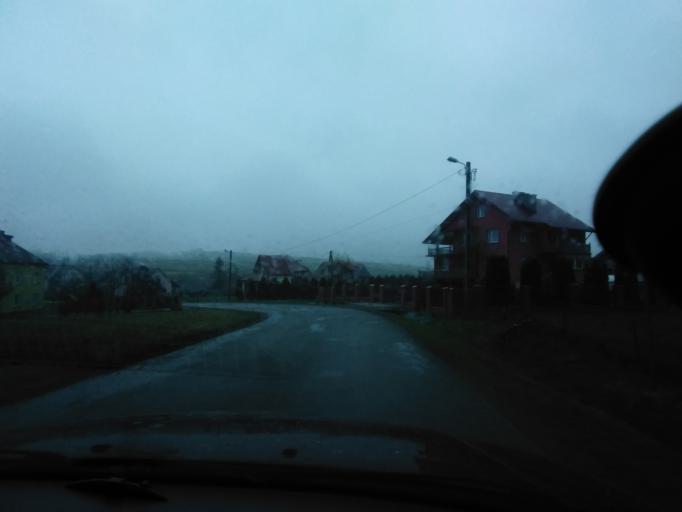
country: PL
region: Subcarpathian Voivodeship
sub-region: Powiat brzozowski
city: Jablonka
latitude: 49.7366
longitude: 22.0963
